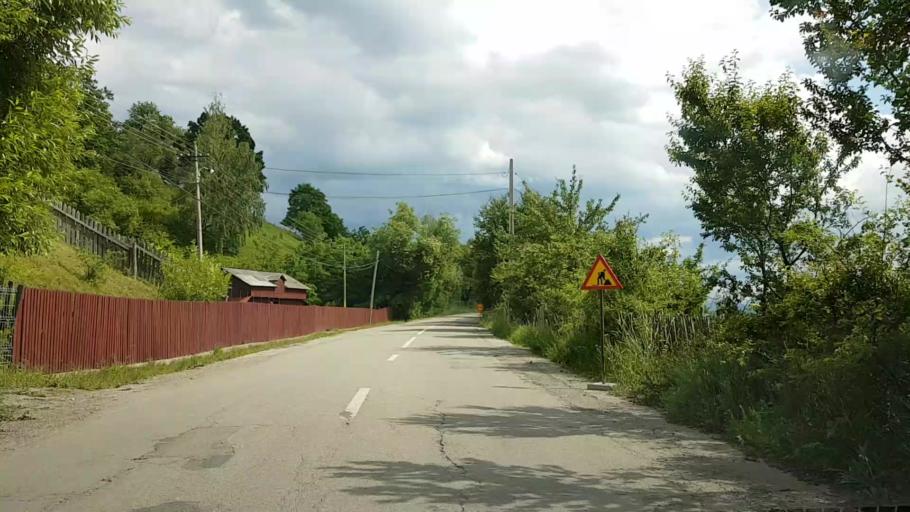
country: RO
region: Neamt
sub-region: Comuna Hangu
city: Hangu
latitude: 47.0413
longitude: 26.0565
